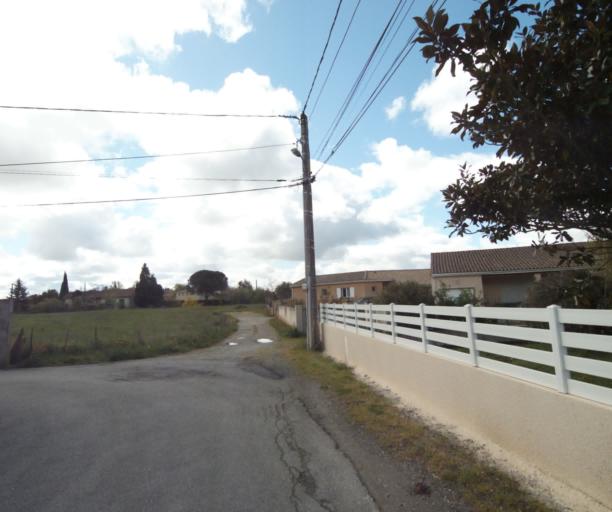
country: FR
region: Midi-Pyrenees
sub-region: Departement de l'Ariege
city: Saverdun
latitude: 43.2278
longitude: 1.5763
